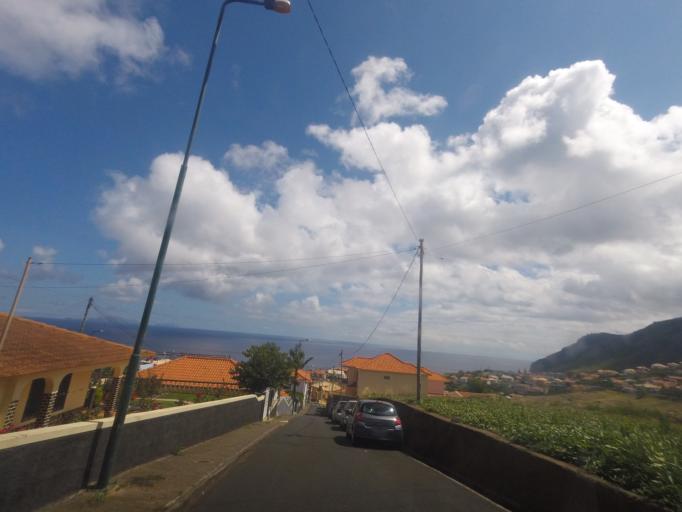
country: PT
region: Madeira
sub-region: Machico
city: Canical
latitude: 32.7442
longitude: -16.7422
